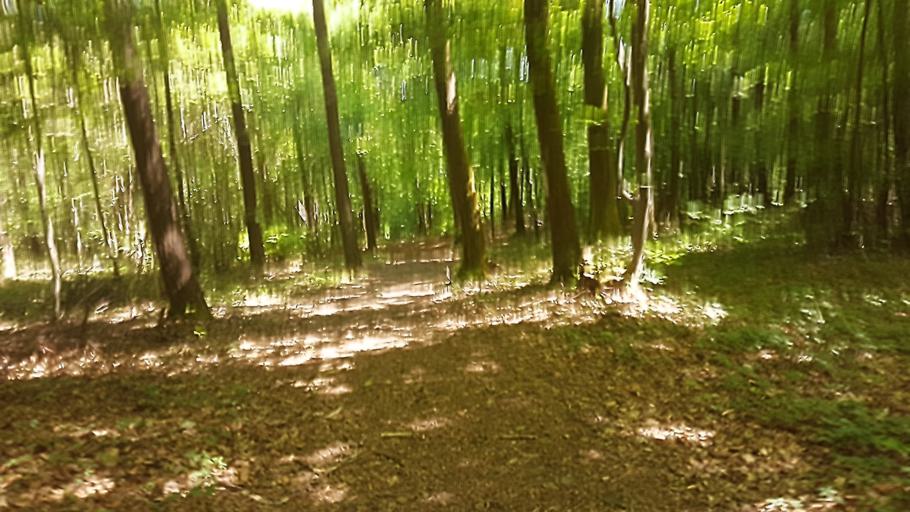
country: BE
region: Wallonia
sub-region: Province de Namur
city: Couvin
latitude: 50.0527
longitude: 4.5837
